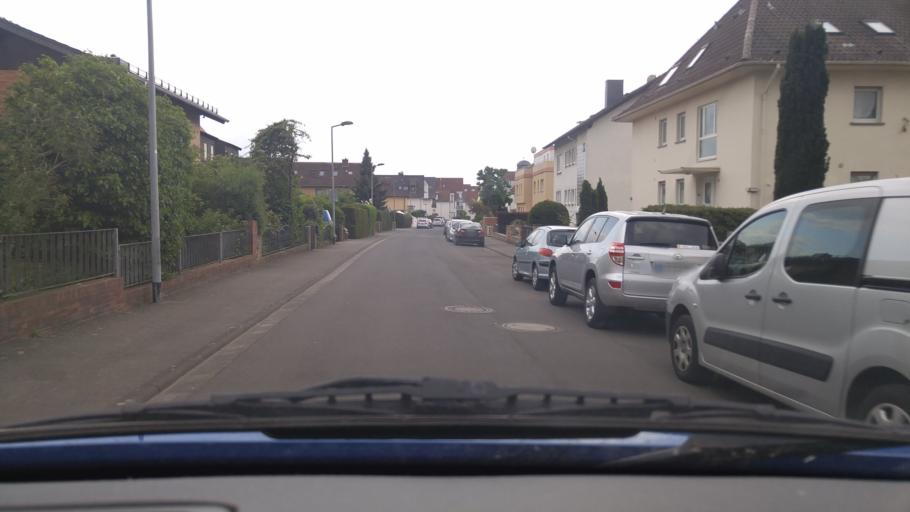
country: DE
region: Hesse
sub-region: Regierungsbezirk Darmstadt
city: Bad Nauheim
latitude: 50.3611
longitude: 8.7498
